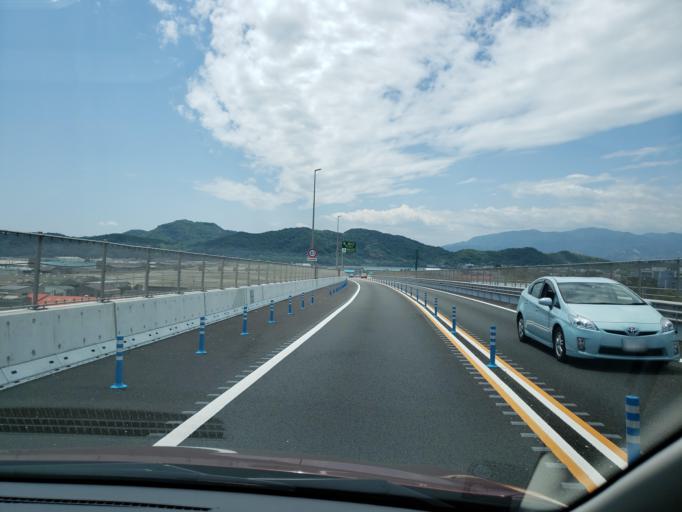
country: JP
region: Tokushima
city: Tokushima-shi
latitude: 34.0497
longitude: 134.5859
